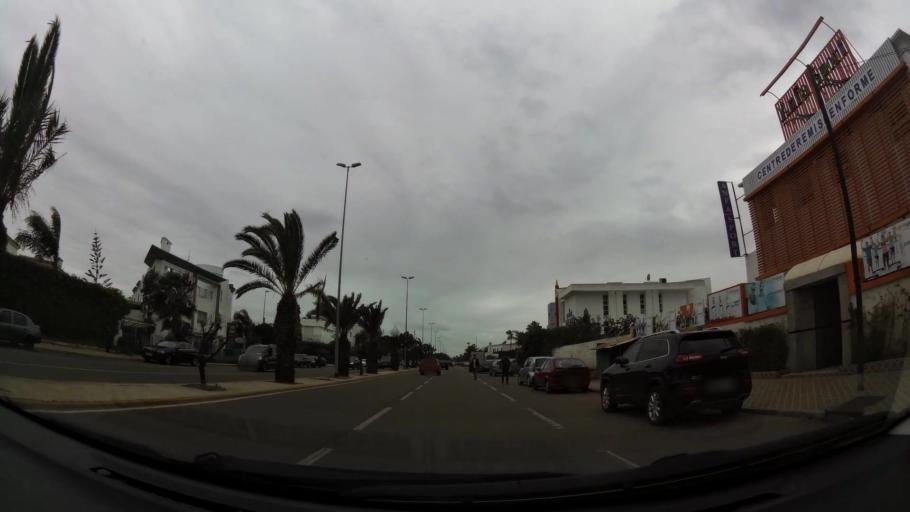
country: MA
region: Grand Casablanca
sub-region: Casablanca
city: Casablanca
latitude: 33.5979
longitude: -7.6550
